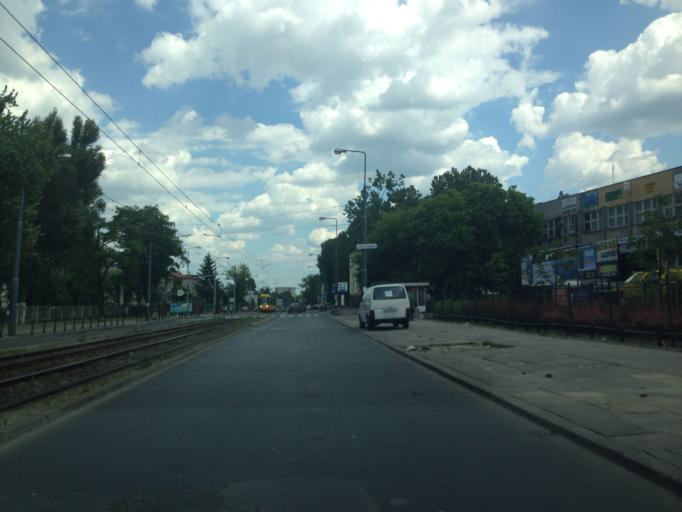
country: PL
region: Masovian Voivodeship
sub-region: Warszawa
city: Bemowo
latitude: 52.2467
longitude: 20.9414
